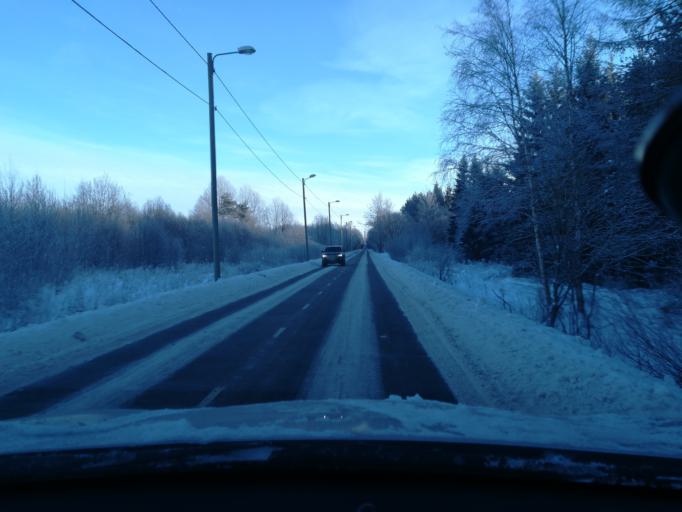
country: EE
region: Harju
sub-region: Saue vald
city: Laagri
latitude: 59.3919
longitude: 24.6079
